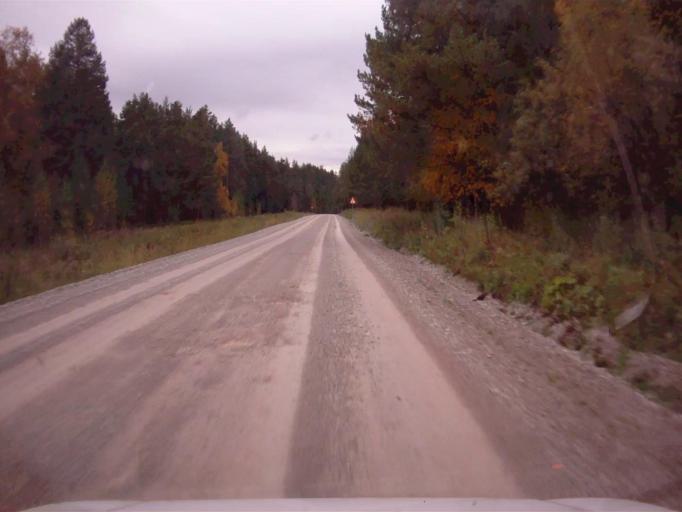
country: RU
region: Chelyabinsk
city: Nyazepetrovsk
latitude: 56.0464
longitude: 59.5220
